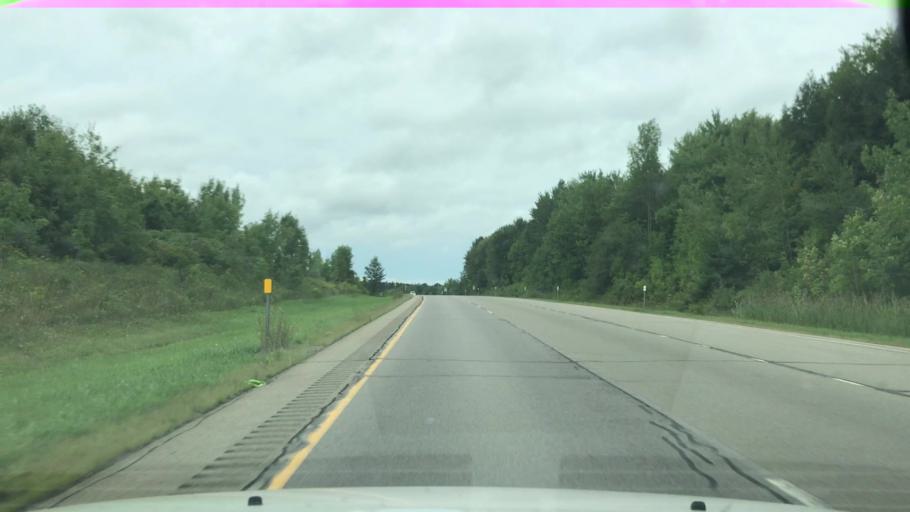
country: US
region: New York
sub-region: Erie County
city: North Boston
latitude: 42.6264
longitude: -78.7648
